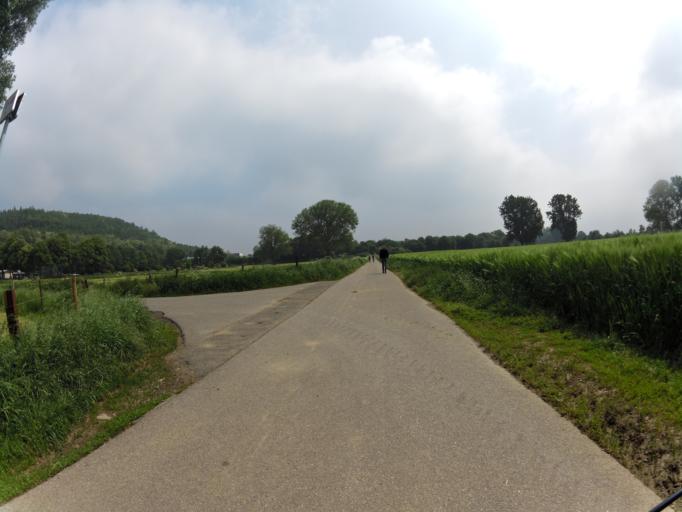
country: DE
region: North Rhine-Westphalia
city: Huckelhoven
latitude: 51.0532
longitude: 6.2018
